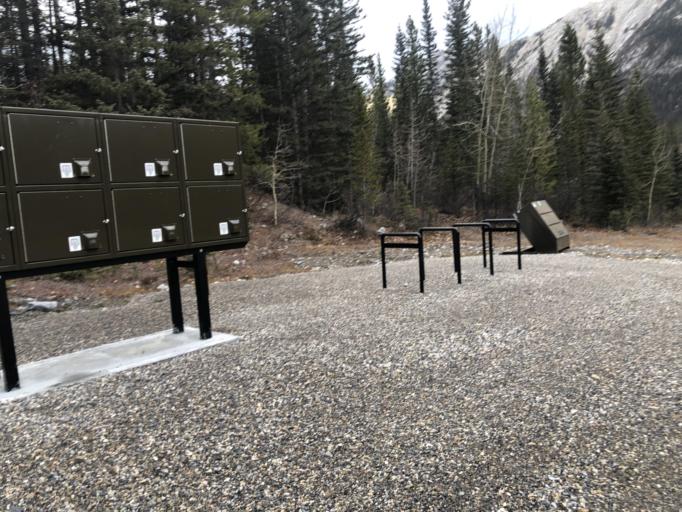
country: CA
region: Alberta
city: Canmore
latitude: 50.9938
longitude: -115.3780
